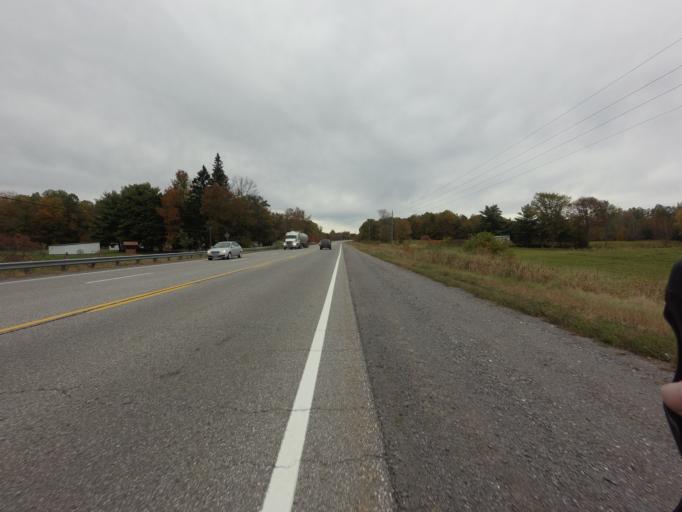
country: CA
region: Ontario
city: Gananoque
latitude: 44.4373
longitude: -76.2827
